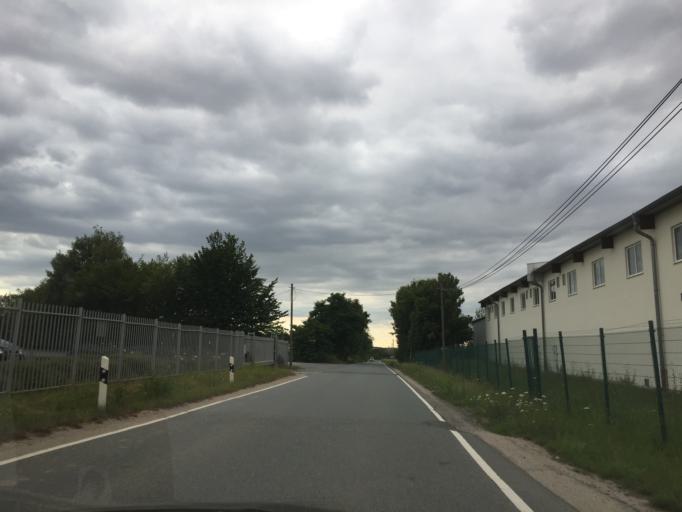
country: DE
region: Thuringia
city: Schmolln
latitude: 50.8750
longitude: 12.3459
